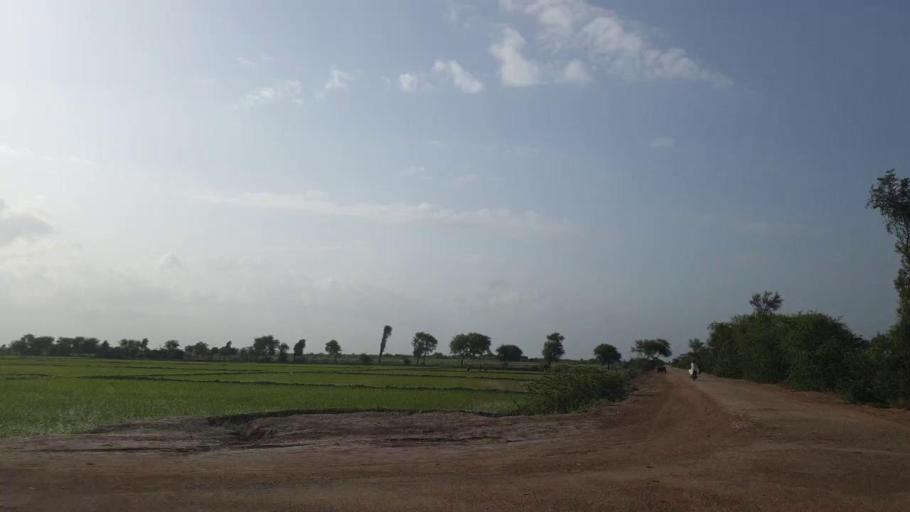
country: PK
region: Sindh
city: Kadhan
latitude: 24.6264
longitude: 69.0959
